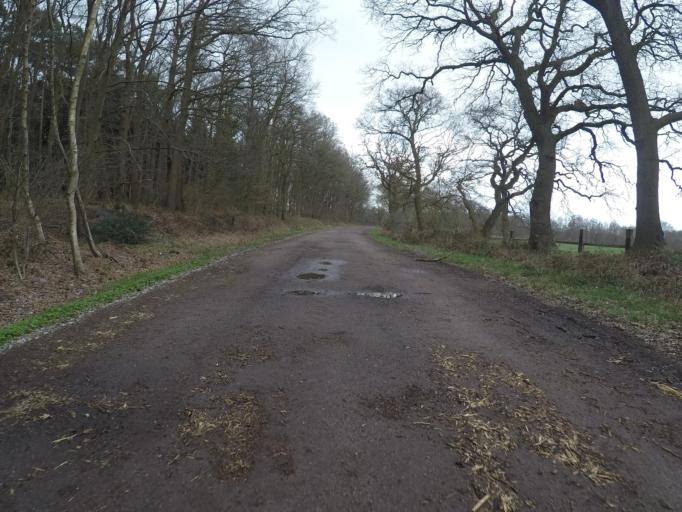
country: DE
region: Lower Saxony
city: Schiffdorf
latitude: 53.6038
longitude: 8.6683
